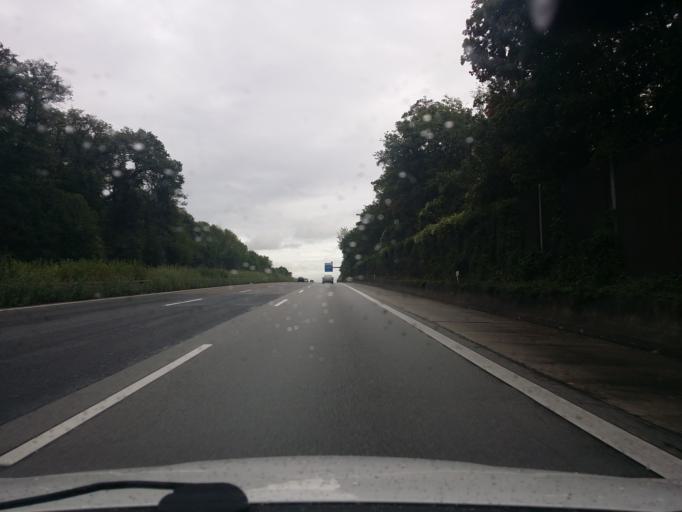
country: DE
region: Hesse
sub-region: Regierungsbezirk Darmstadt
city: Niedernhausen
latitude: 50.1093
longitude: 8.3452
